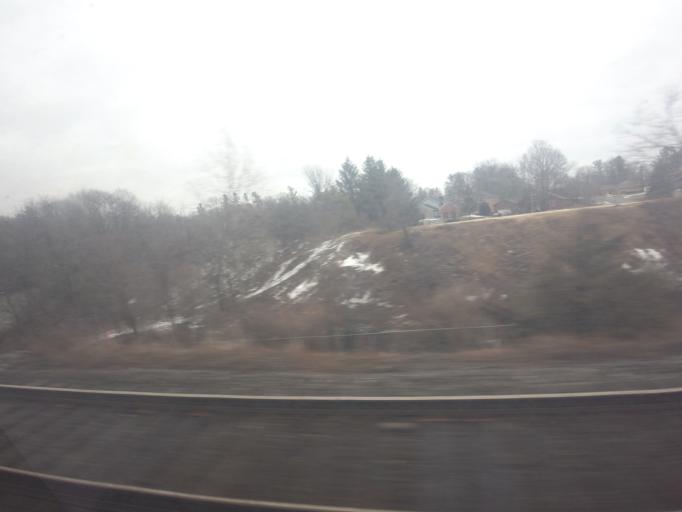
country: CA
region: Ontario
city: Kingston
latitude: 44.2395
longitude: -76.6217
